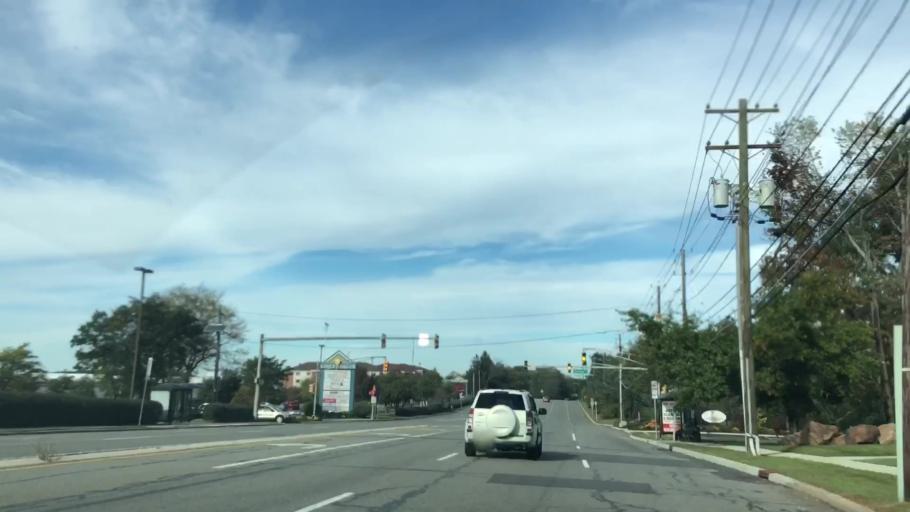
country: US
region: New Jersey
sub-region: Essex County
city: West Orange
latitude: 40.7920
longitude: -74.2543
